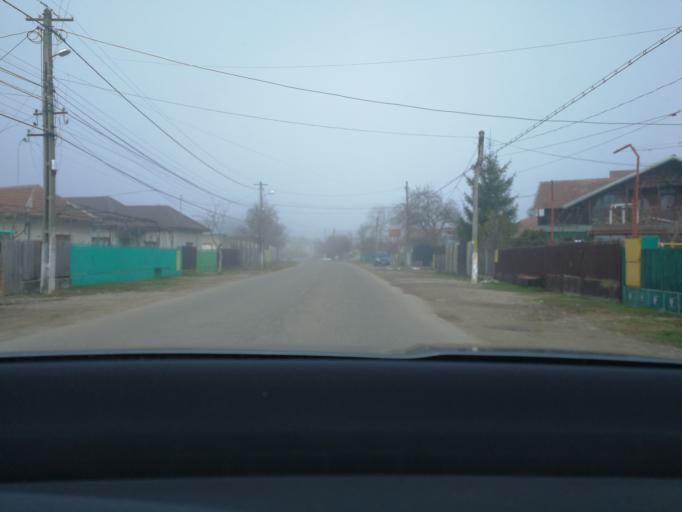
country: RO
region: Prahova
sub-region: Comuna Magureni
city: Lunca Prahovei
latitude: 45.0397
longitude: 25.7555
